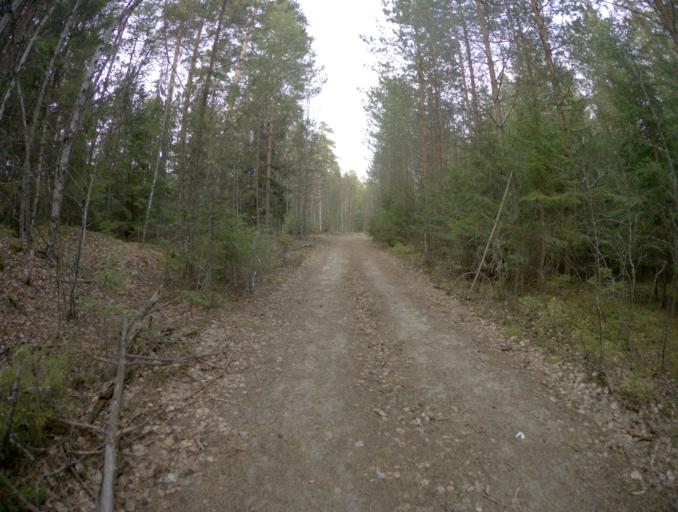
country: RU
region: Vladimir
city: Kommunar
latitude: 56.0749
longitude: 40.5180
